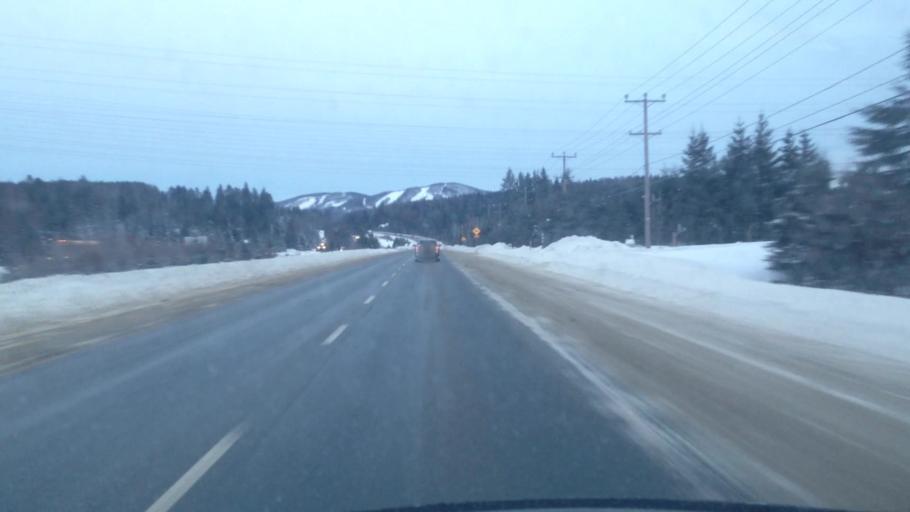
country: CA
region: Quebec
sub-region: Laurentides
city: Mont-Tremblant
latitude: 46.1153
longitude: -74.5488
